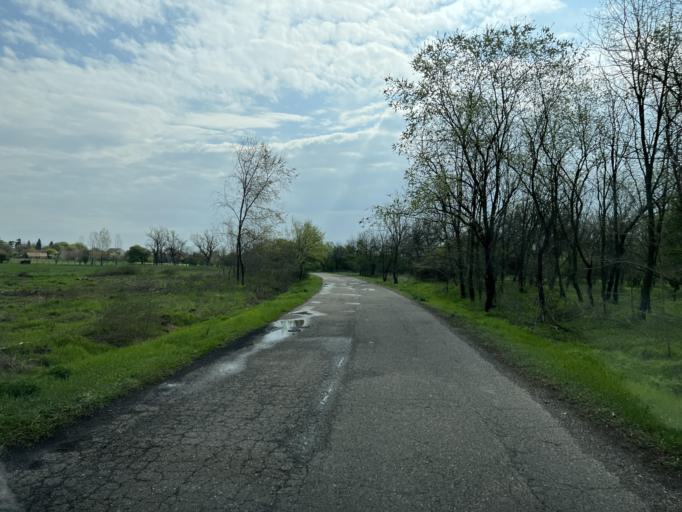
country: HU
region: Pest
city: Hernad
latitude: 47.1711
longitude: 19.4899
